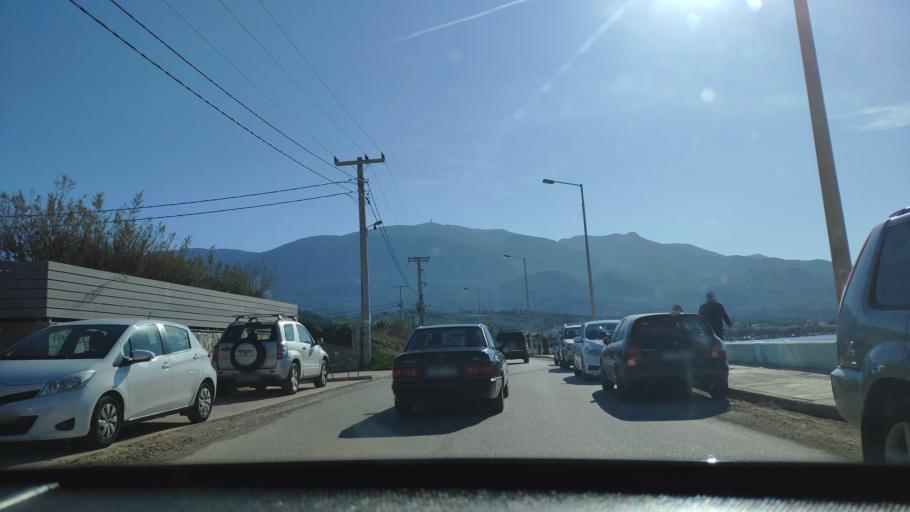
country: GR
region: Attica
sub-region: Nomarchia Dytikis Attikis
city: Kineta
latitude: 38.0772
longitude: 23.1740
